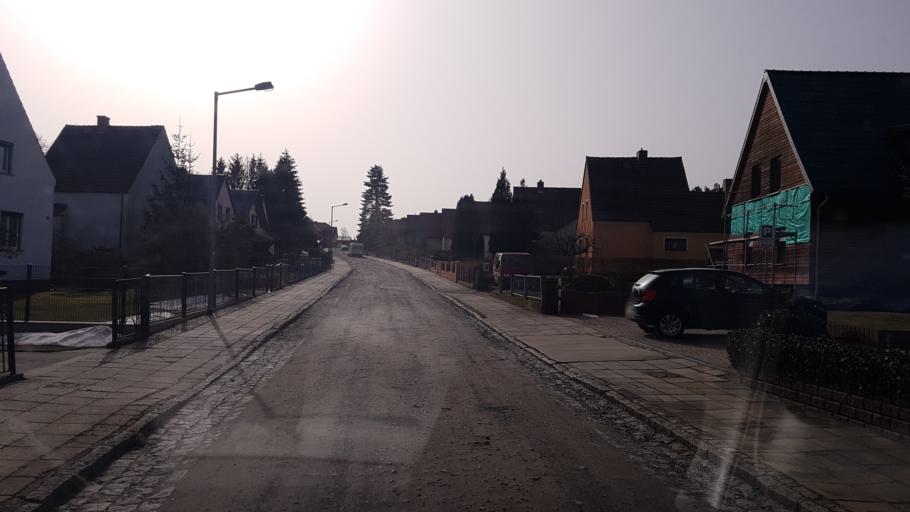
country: DE
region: Brandenburg
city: Lauchhammer
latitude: 51.5078
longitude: 13.7925
